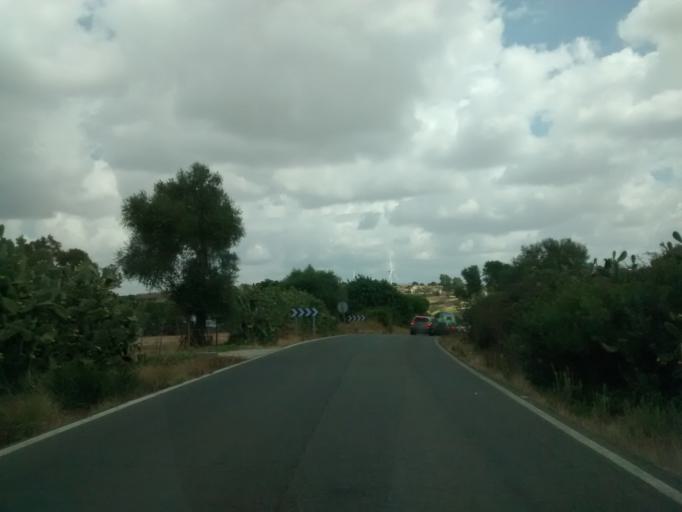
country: ES
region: Andalusia
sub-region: Provincia de Cadiz
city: Medina Sidonia
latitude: 36.4903
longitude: -5.9007
